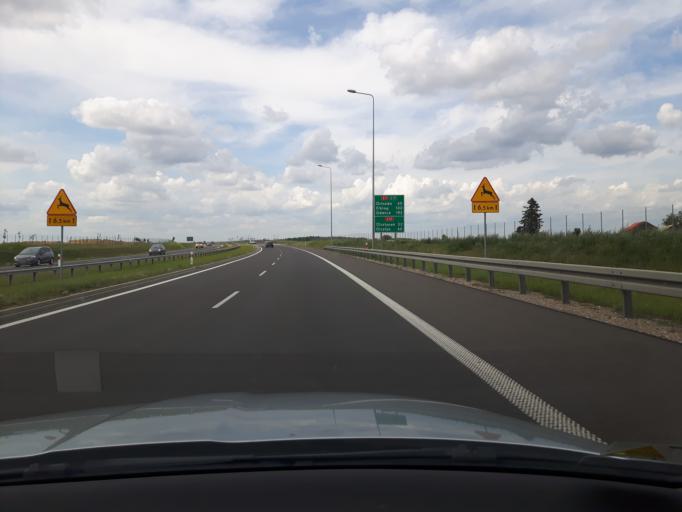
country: PL
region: Warmian-Masurian Voivodeship
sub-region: Powiat nidzicki
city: Nidzica
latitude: 53.3354
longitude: 20.4338
